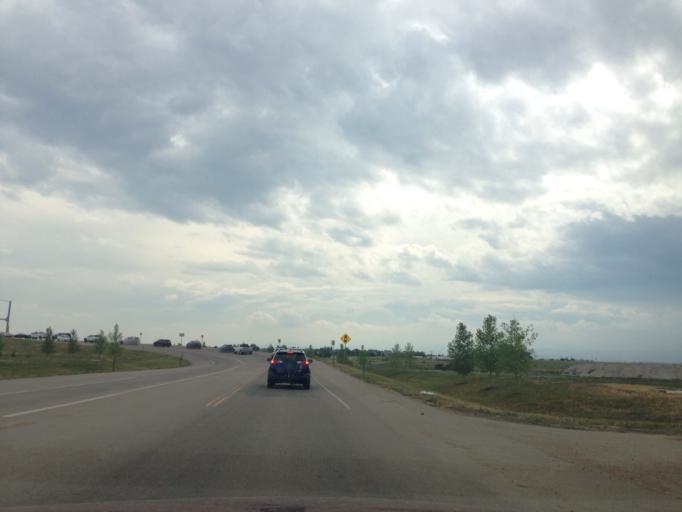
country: US
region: Colorado
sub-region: Weld County
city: Windsor
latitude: 40.4813
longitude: -104.9933
